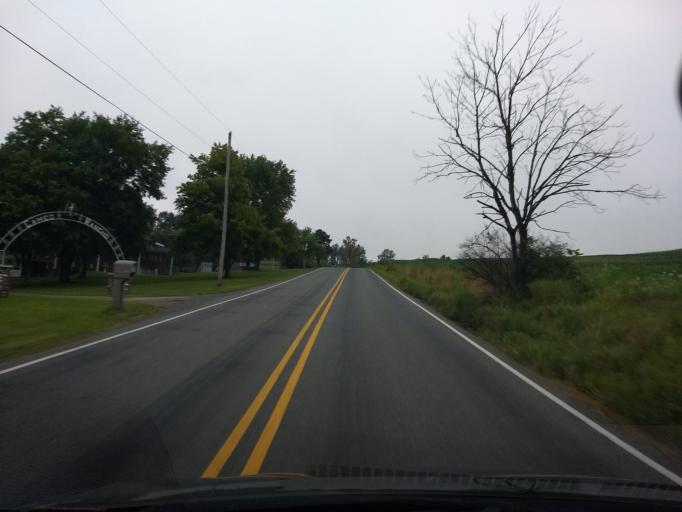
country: US
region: Pennsylvania
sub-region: Westmoreland County
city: Greensburg
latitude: 40.3316
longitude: -79.4874
